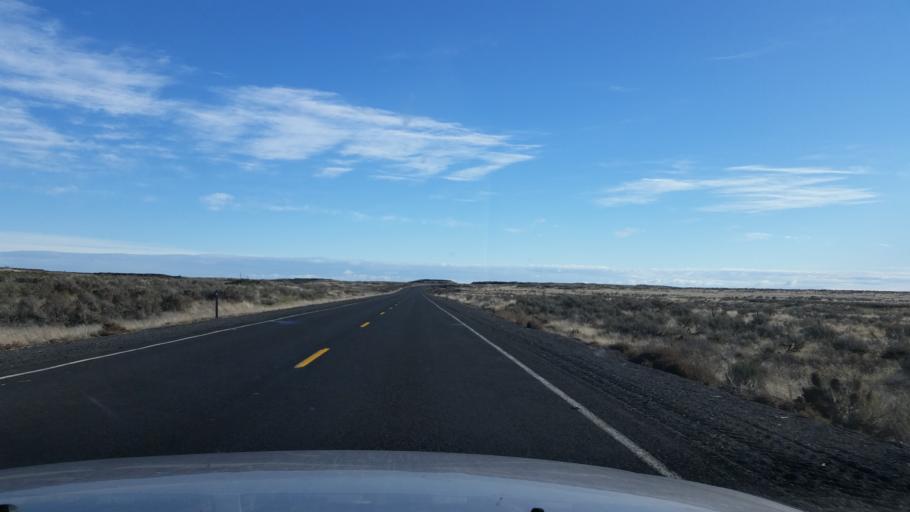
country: US
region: Washington
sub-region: Grant County
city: Warden
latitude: 47.3321
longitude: -118.8839
